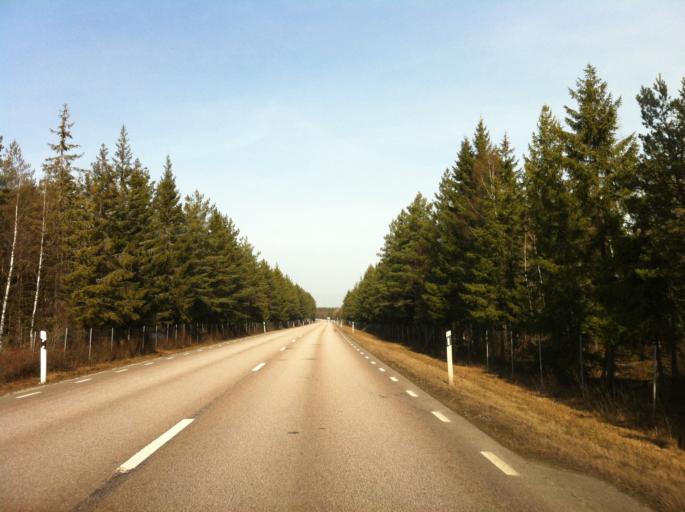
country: SE
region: Vaestra Goetaland
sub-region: Tidaholms Kommun
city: Tidaholm
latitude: 58.1077
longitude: 13.8876
